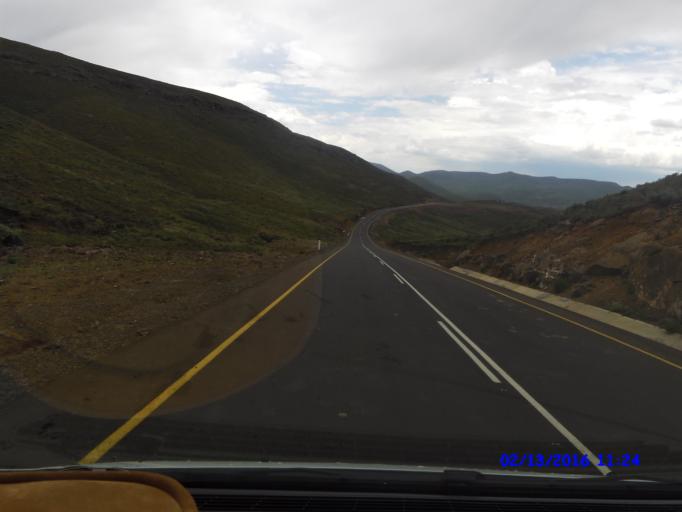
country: LS
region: Maseru
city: Nako
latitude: -29.7653
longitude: 27.9986
